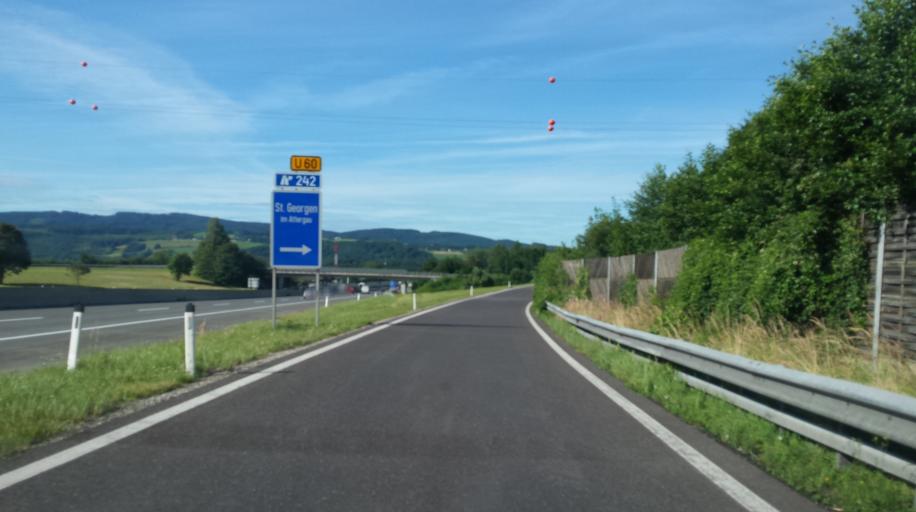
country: AT
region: Upper Austria
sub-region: Politischer Bezirk Vocklabruck
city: Sankt Georgen im Attergau
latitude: 47.9309
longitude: 13.5112
